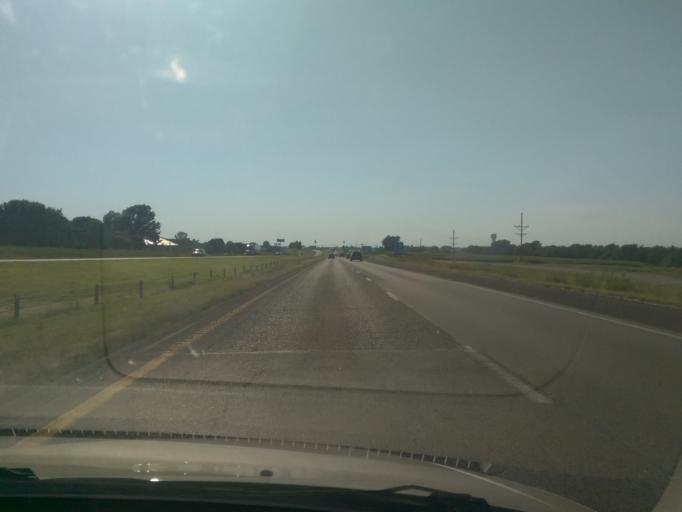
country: US
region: Missouri
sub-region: Lafayette County
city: Concordia
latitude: 38.9894
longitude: -93.5512
